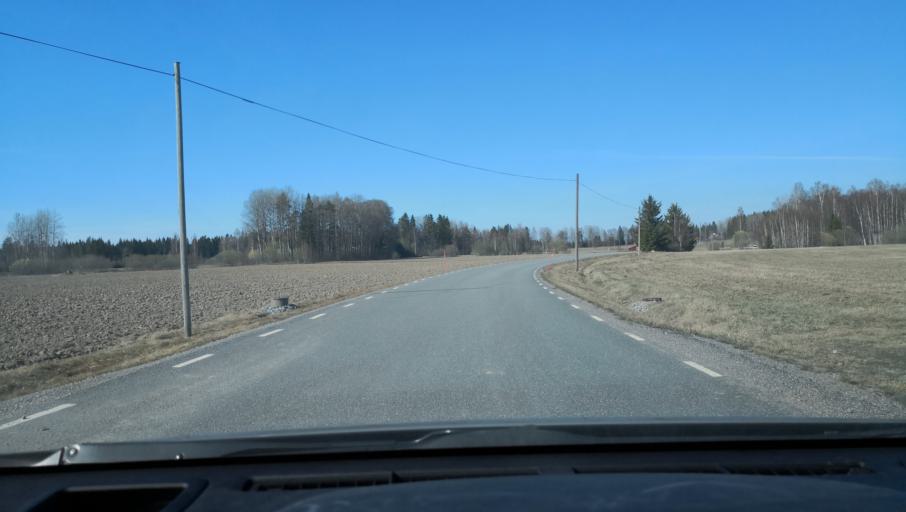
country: SE
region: Vaestmanland
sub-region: Sala Kommun
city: Sala
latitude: 59.9667
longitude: 16.4617
